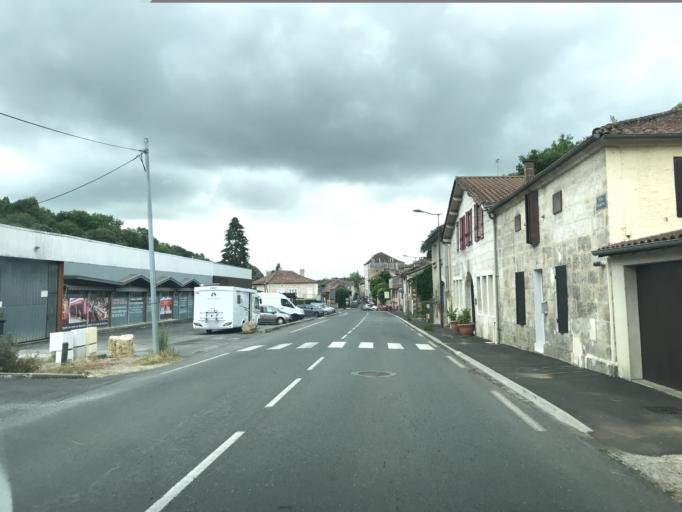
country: FR
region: Aquitaine
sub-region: Departement de la Dordogne
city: Brantome
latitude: 45.3686
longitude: 0.6478
